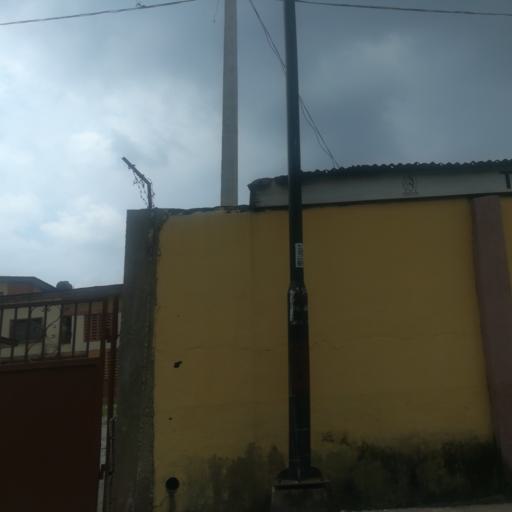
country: NG
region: Lagos
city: Ojota
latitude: 6.5822
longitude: 3.3828
